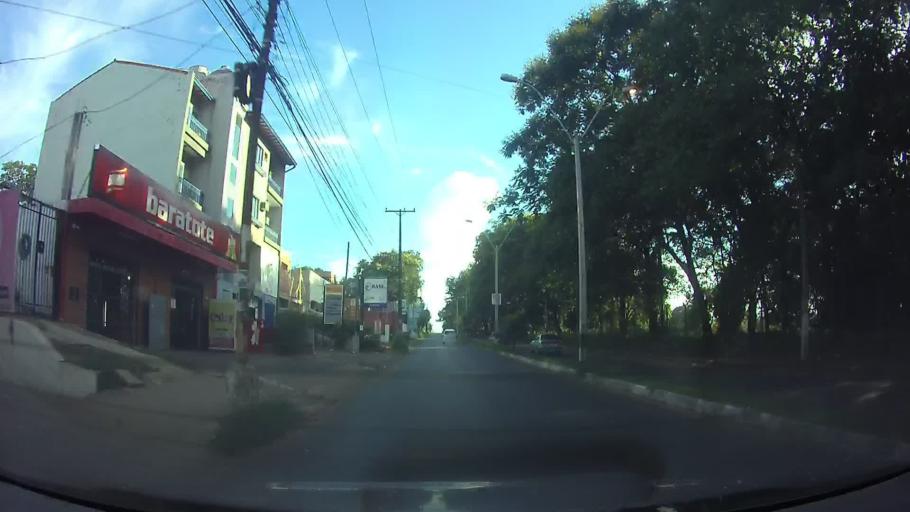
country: PY
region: Central
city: Villa Elisa
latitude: -25.3715
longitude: -57.5842
